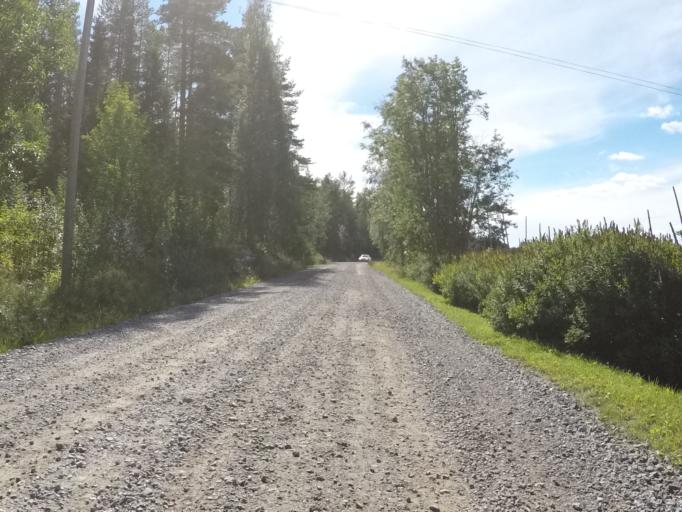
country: SE
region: Vaesterbotten
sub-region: Robertsfors Kommun
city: Robertsfors
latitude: 64.0093
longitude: 20.8176
